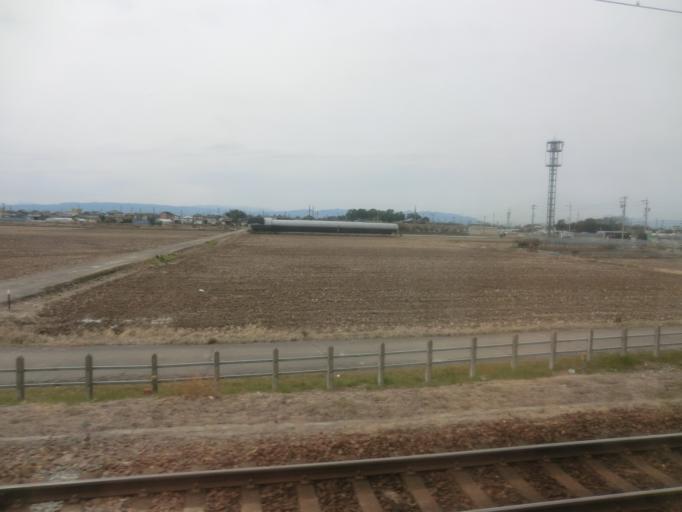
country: JP
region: Aichi
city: Ichinomiya
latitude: 35.2713
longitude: 136.8118
